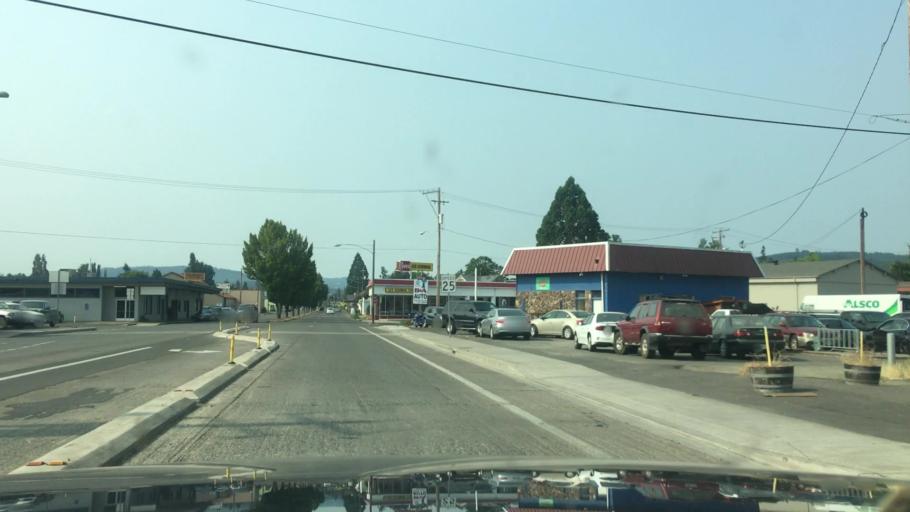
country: US
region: Oregon
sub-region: Lane County
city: Cottage Grove
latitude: 43.7970
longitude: -123.0593
